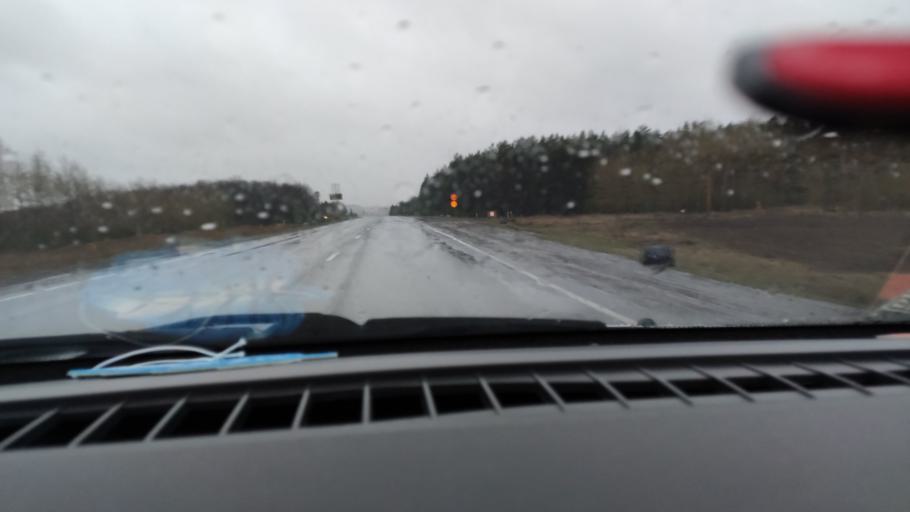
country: RU
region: Tatarstan
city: Mendeleyevsk
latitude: 55.9467
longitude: 52.2976
